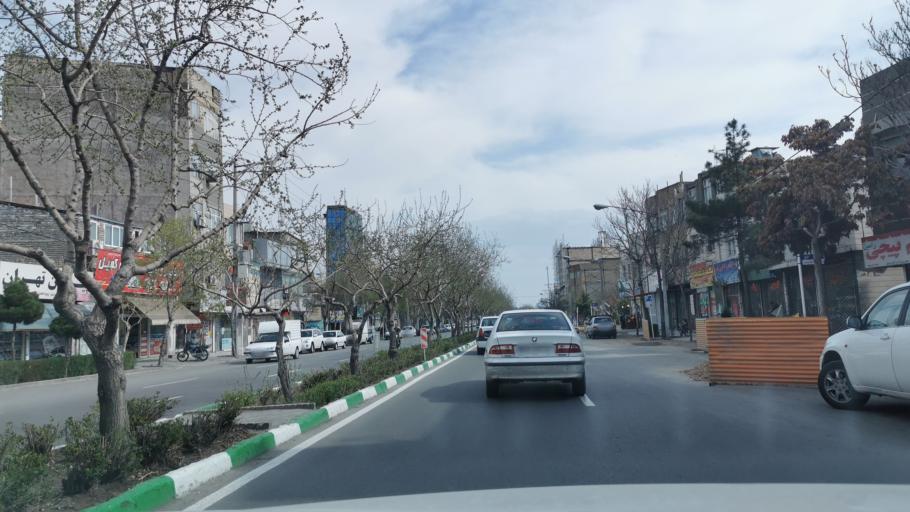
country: IR
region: Razavi Khorasan
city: Mashhad
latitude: 36.3137
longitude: 59.6121
